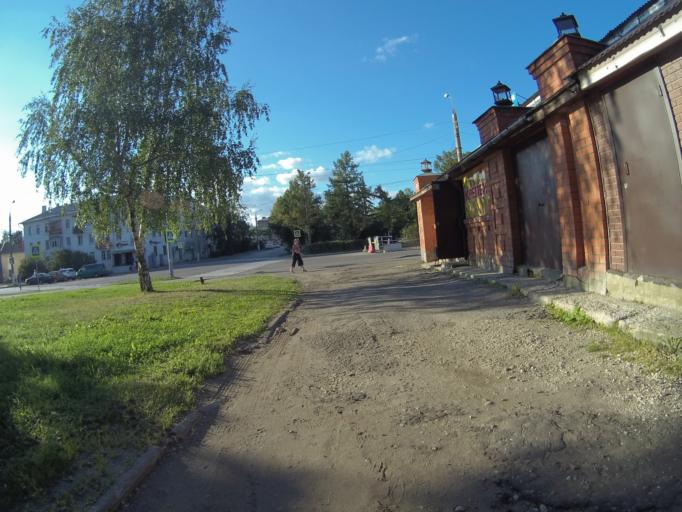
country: RU
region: Vladimir
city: Vladimir
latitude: 56.1213
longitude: 40.3635
